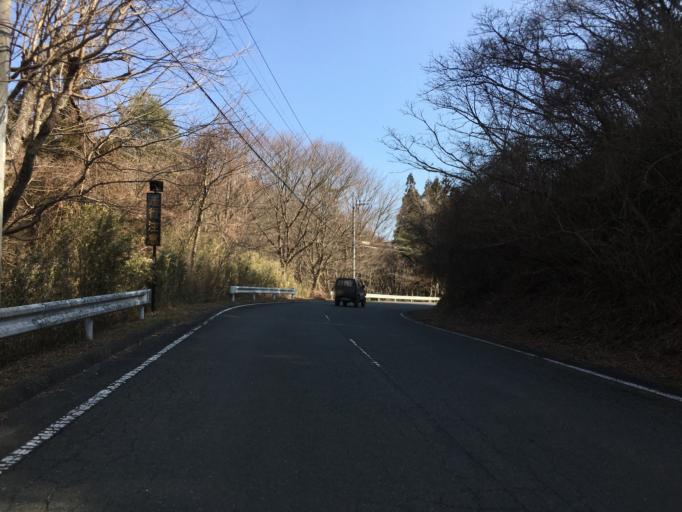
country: JP
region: Ibaraki
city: Takahagi
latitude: 36.8180
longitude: 140.5772
